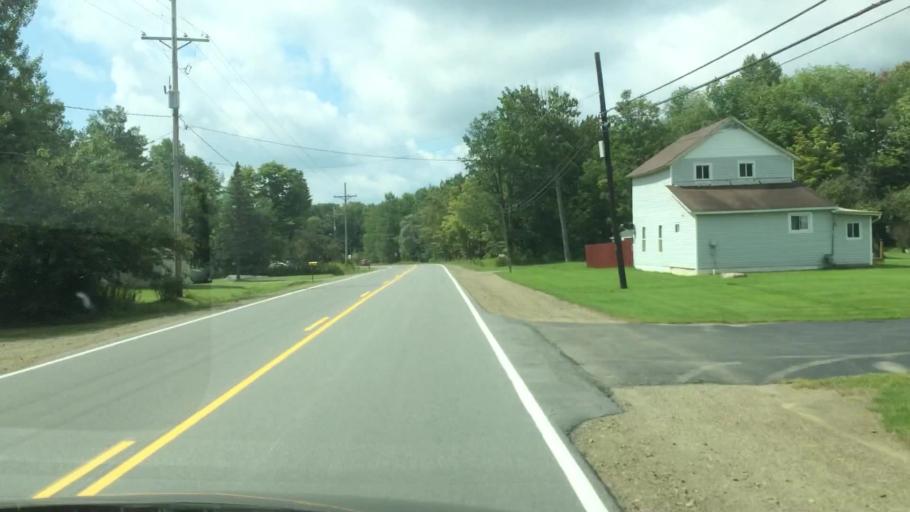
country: US
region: Pennsylvania
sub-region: McKean County
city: Bradford
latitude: 41.8732
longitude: -78.5869
